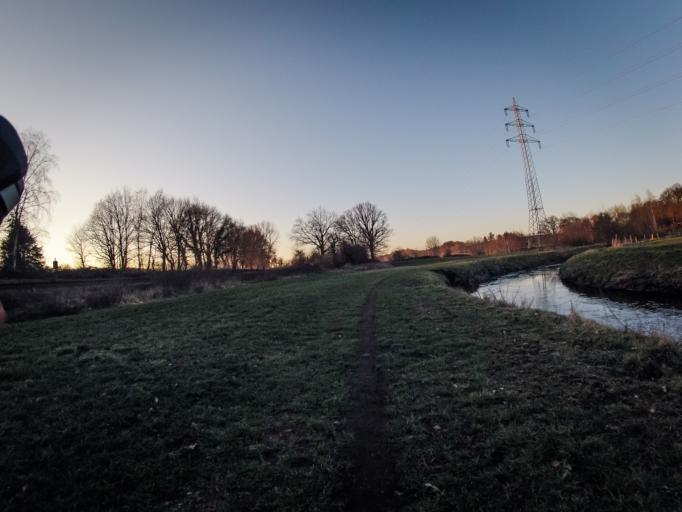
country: DE
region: Lower Saxony
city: Wallenhorst
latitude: 52.3125
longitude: 7.9766
